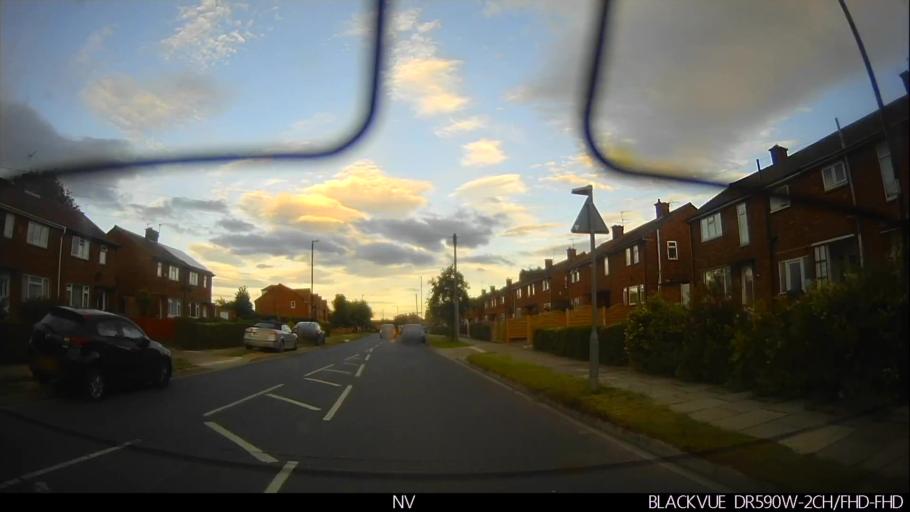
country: GB
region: England
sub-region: City of York
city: Bishopthorpe
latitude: 53.9427
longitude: -1.1189
